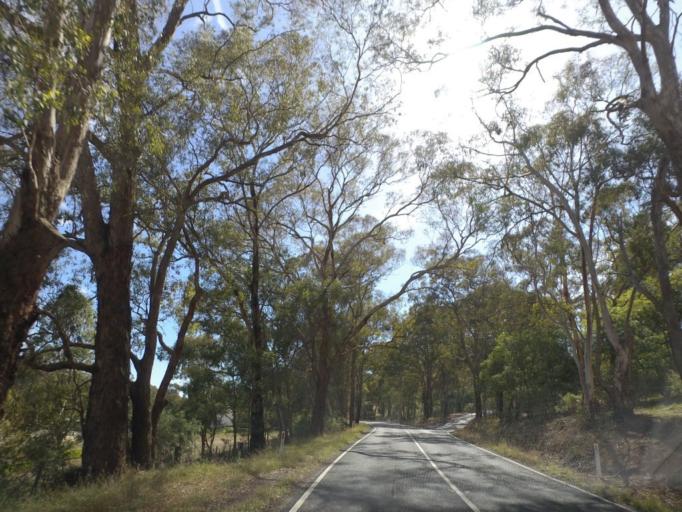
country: AU
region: Victoria
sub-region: Nillumbik
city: Hurstbridge
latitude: -37.6318
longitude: 145.2077
